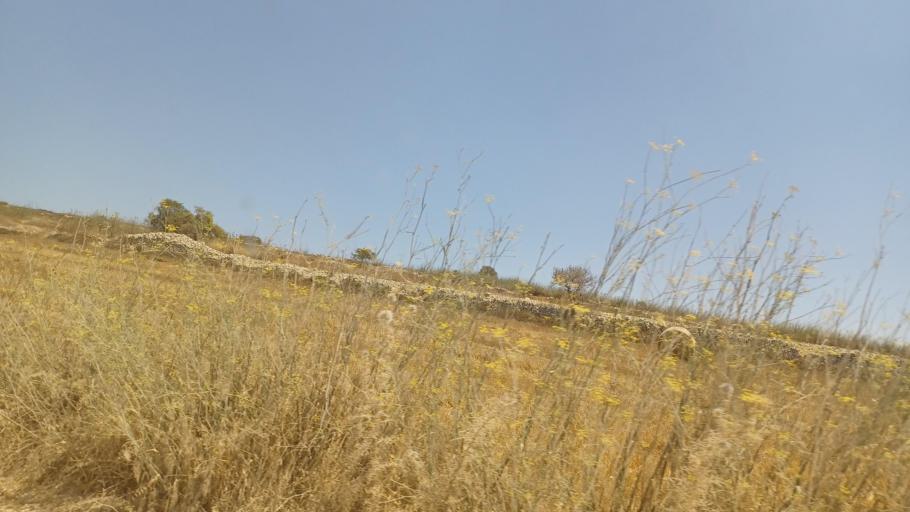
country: CY
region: Pafos
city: Pegeia
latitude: 34.9478
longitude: 32.4048
